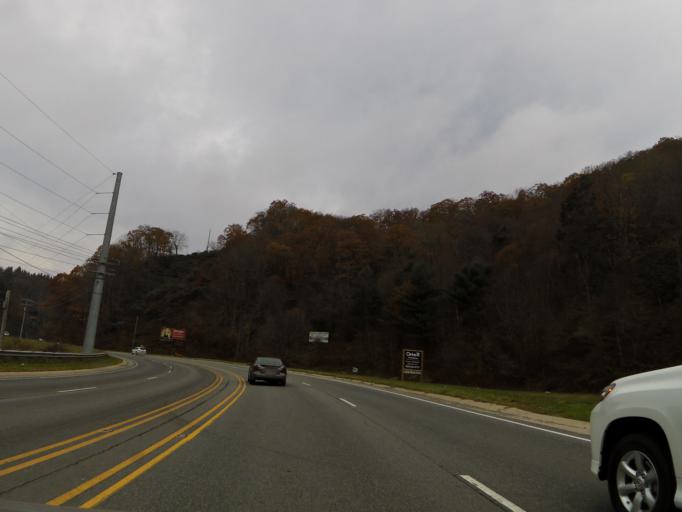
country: US
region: North Carolina
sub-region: Watauga County
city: Blowing Rock
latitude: 36.1530
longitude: -81.6506
